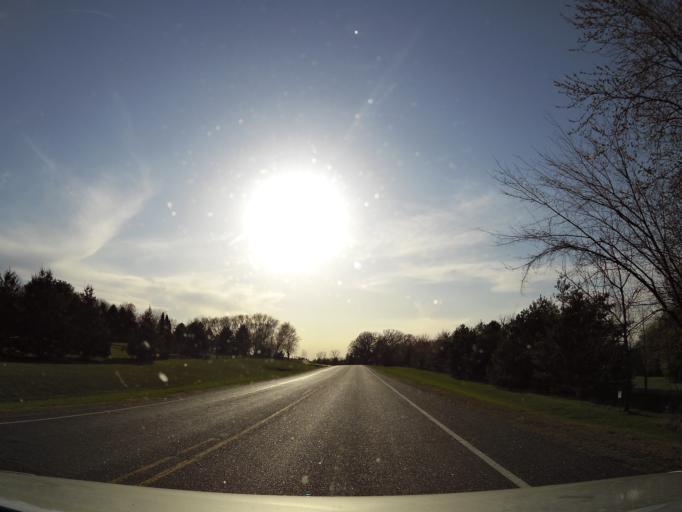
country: US
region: Minnesota
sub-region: Washington County
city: Afton
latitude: 44.8256
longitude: -92.7290
